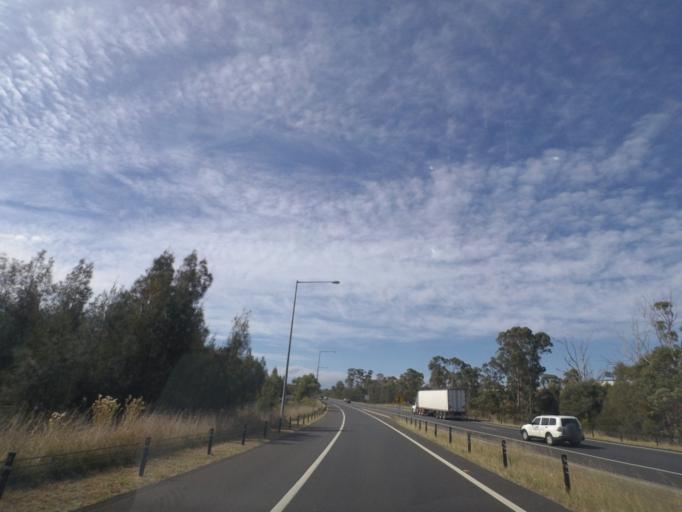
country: AU
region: New South Wales
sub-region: Campbelltown Municipality
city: Glenfield
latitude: -33.9522
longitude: 150.8770
